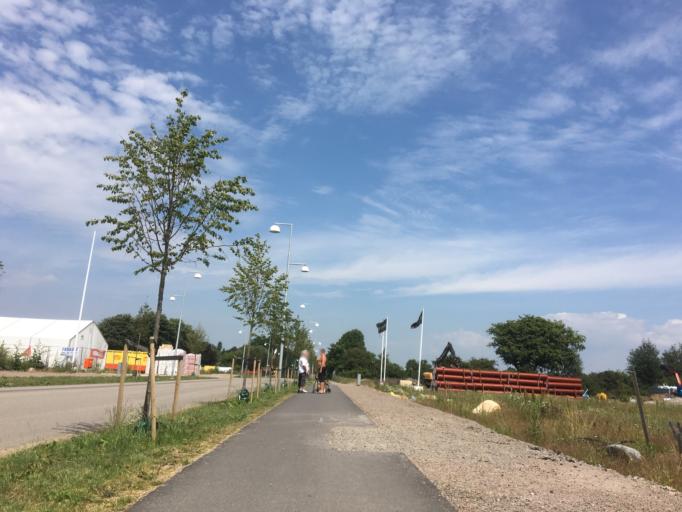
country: SE
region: Skane
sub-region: Landskrona
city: Landskrona
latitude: 55.9001
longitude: 12.8069
